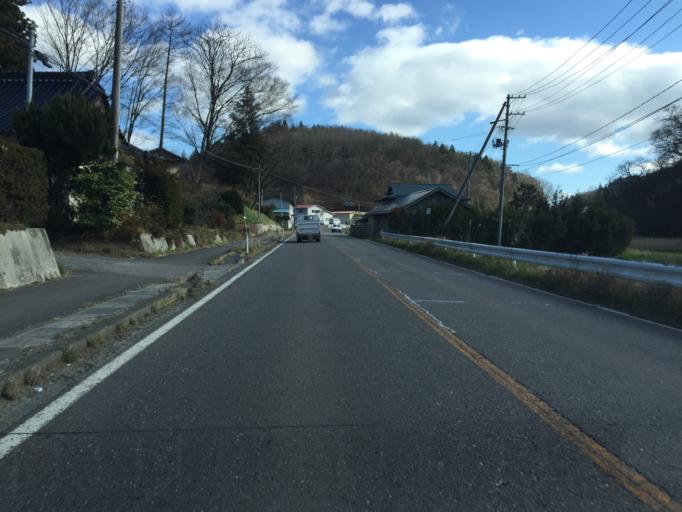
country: JP
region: Fukushima
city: Ishikawa
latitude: 37.2342
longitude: 140.5751
